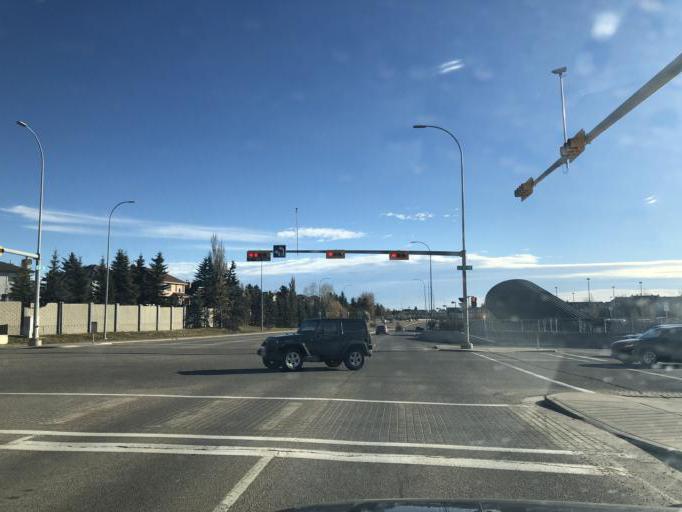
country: CA
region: Alberta
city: Calgary
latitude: 51.0378
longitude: -114.1881
